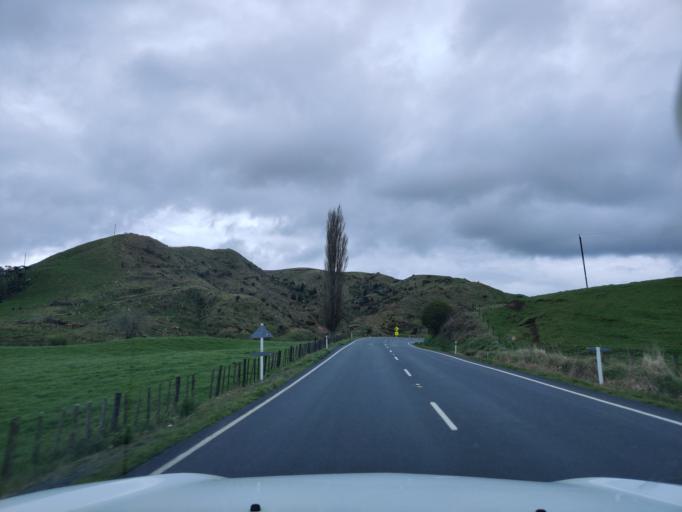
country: NZ
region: Waikato
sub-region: Otorohanga District
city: Otorohanga
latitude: -38.5191
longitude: 175.1955
